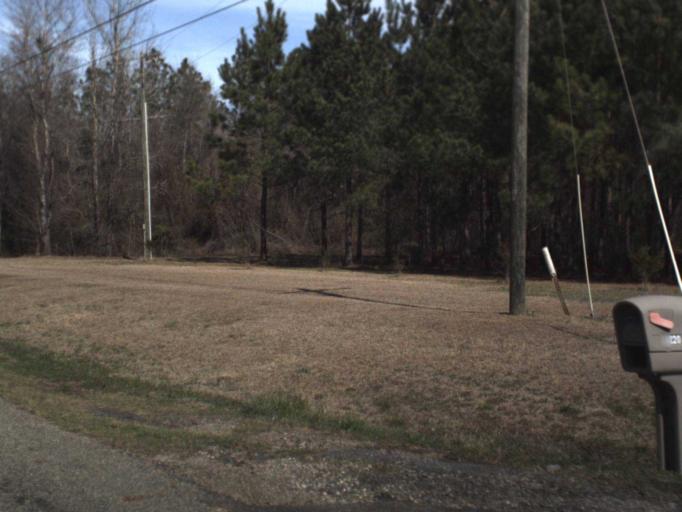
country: US
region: Florida
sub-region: Jackson County
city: Graceville
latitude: 30.8752
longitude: -85.5259
